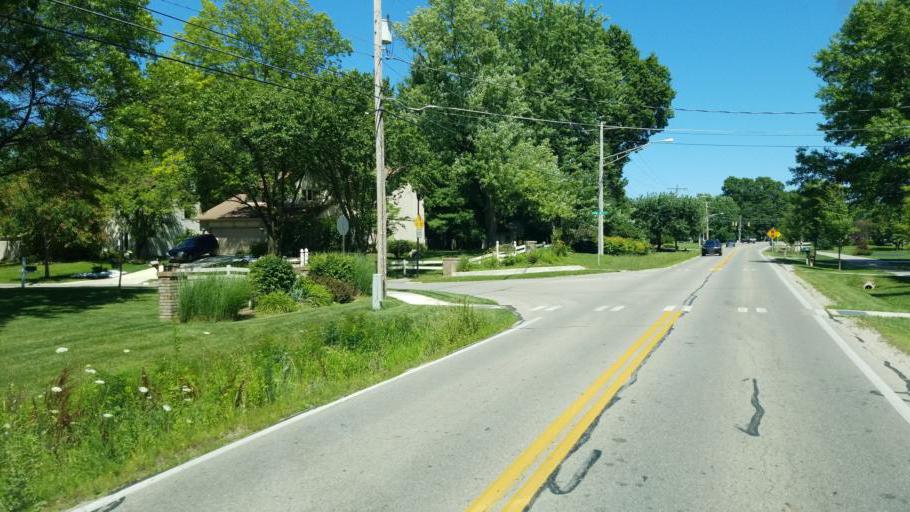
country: US
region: Ohio
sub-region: Franklin County
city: Westerville
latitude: 40.1203
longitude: -82.8952
